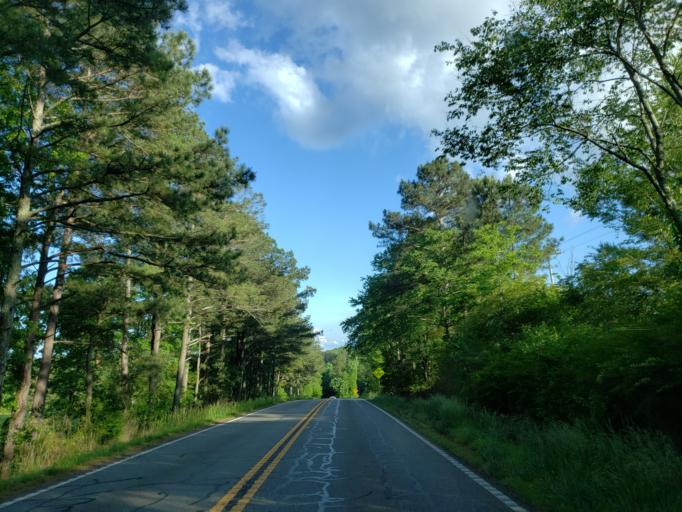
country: US
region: Georgia
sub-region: Bartow County
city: Rydal
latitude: 34.3438
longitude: -84.5783
